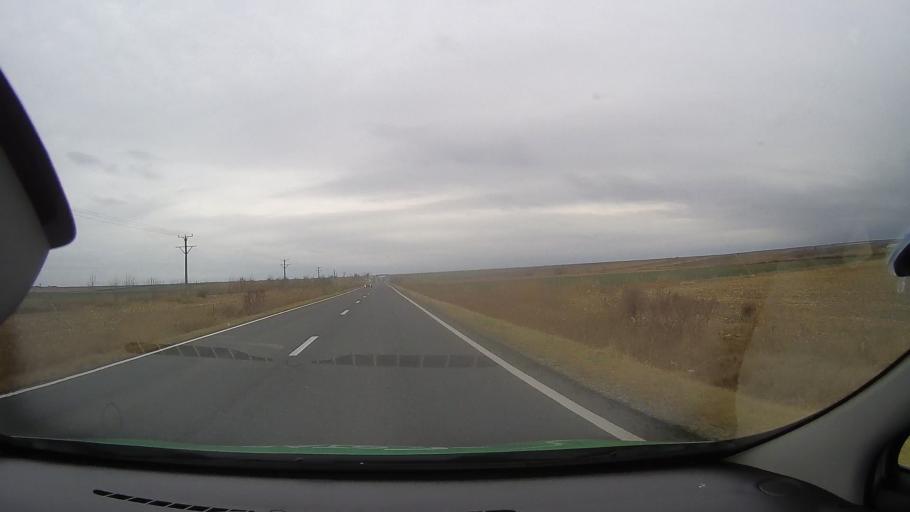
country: RO
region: Constanta
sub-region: Comuna Nicolae Balcescu
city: Nicolae Balcescu
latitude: 44.3853
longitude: 28.3929
